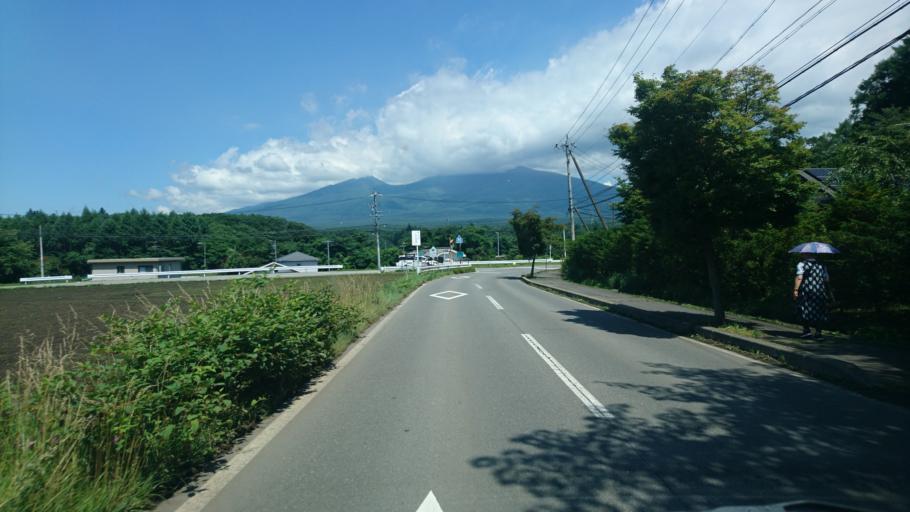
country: JP
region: Nagano
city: Saku
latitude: 36.3284
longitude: 138.5860
